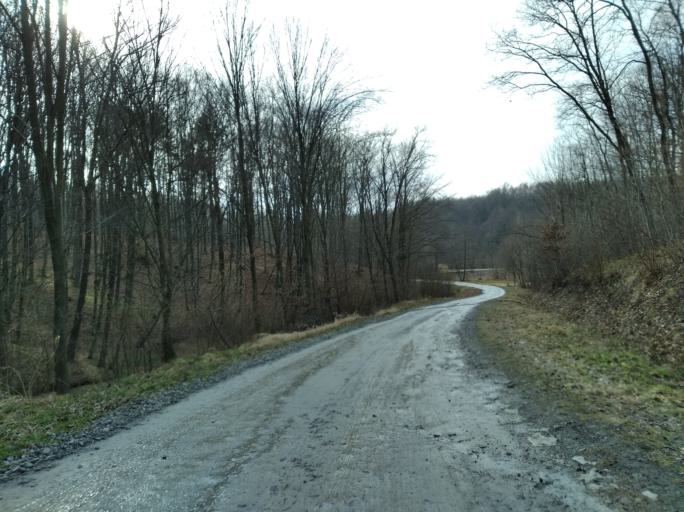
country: PL
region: Subcarpathian Voivodeship
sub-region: Powiat brzozowski
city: Gorki
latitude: 49.6386
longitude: 22.0588
